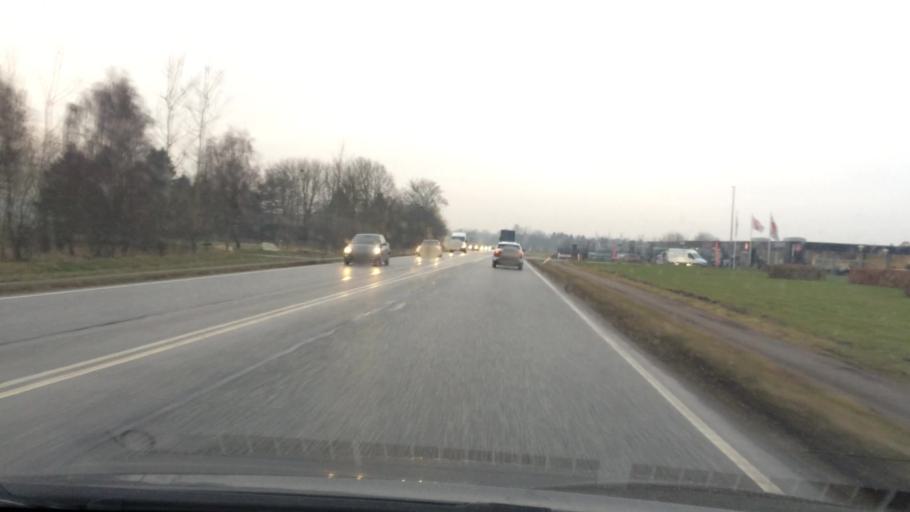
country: DK
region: Central Jutland
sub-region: Horsens Kommune
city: Horsens
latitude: 55.8278
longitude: 9.7990
